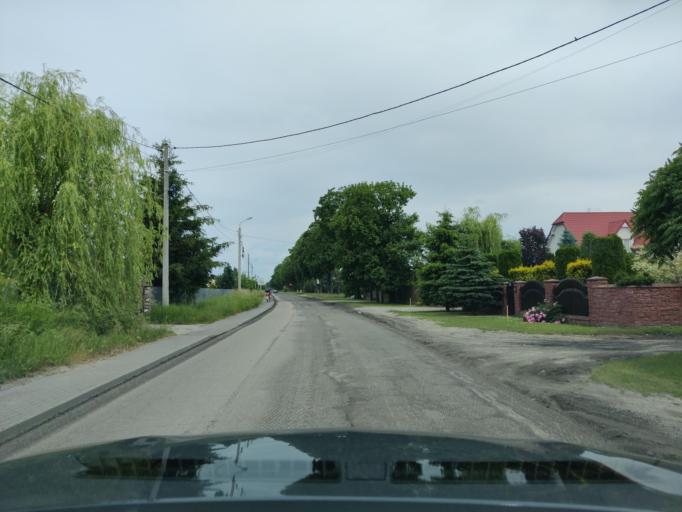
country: PL
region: Masovian Voivodeship
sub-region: Powiat wyszkowski
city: Rzasnik
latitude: 52.6898
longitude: 21.4214
